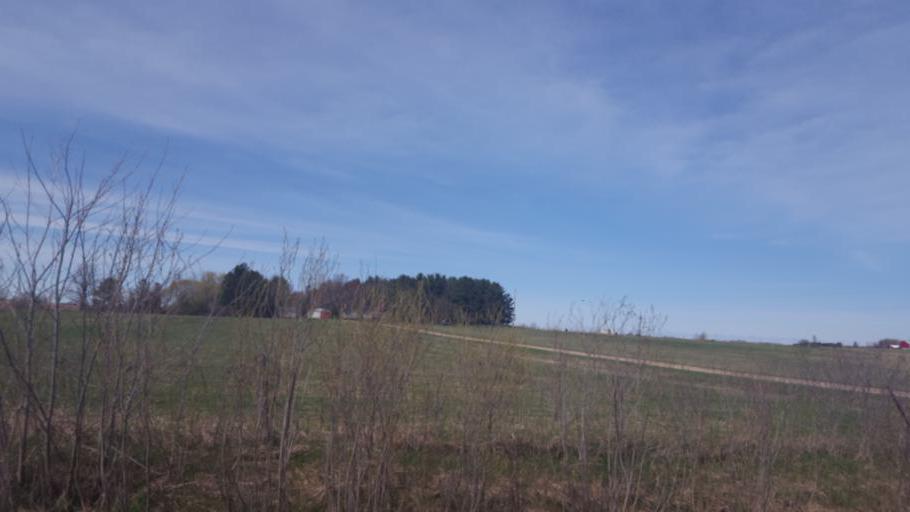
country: US
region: Michigan
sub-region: Gladwin County
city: Gladwin
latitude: 44.0599
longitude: -84.4770
